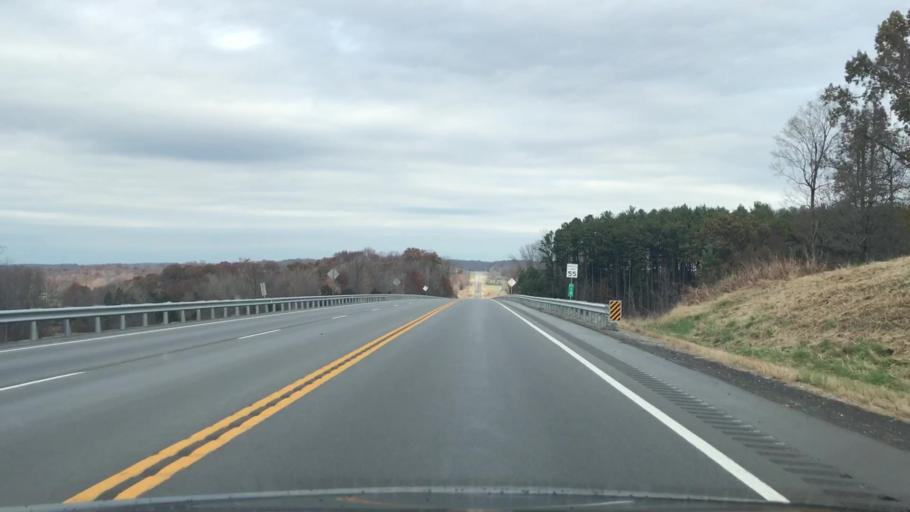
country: US
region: Kentucky
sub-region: Monroe County
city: Tompkinsville
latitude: 36.7920
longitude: -85.6869
